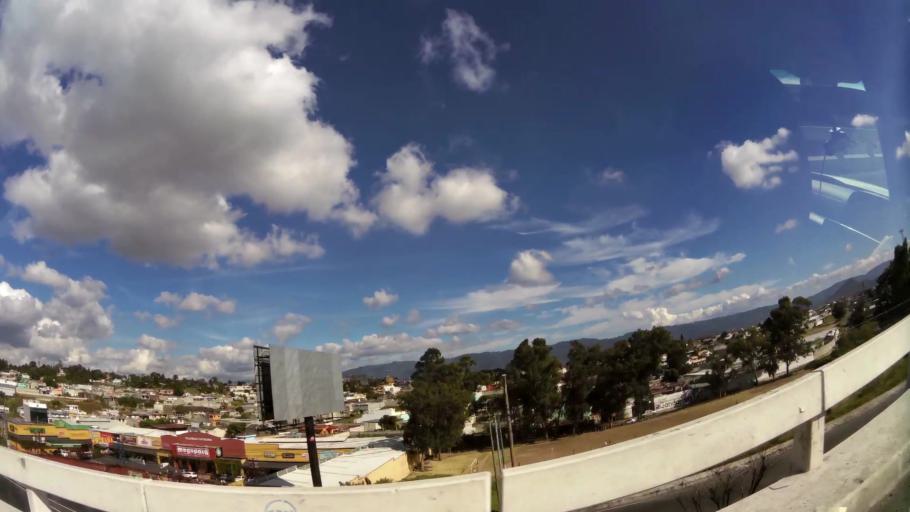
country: GT
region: Guatemala
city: Villa Nueva
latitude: 14.5378
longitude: -90.5852
